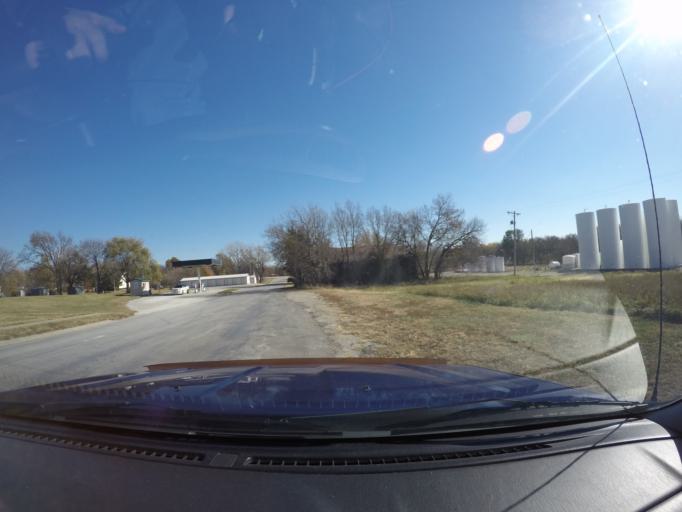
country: US
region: Kansas
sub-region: Marshall County
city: Marysville
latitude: 39.8604
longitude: -96.4169
